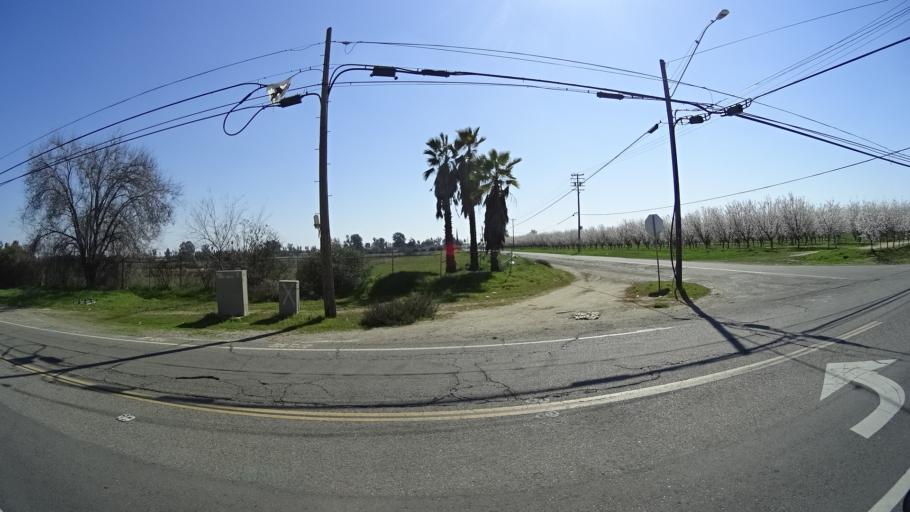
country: US
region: California
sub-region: Fresno County
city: West Park
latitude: 36.7357
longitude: -119.8355
